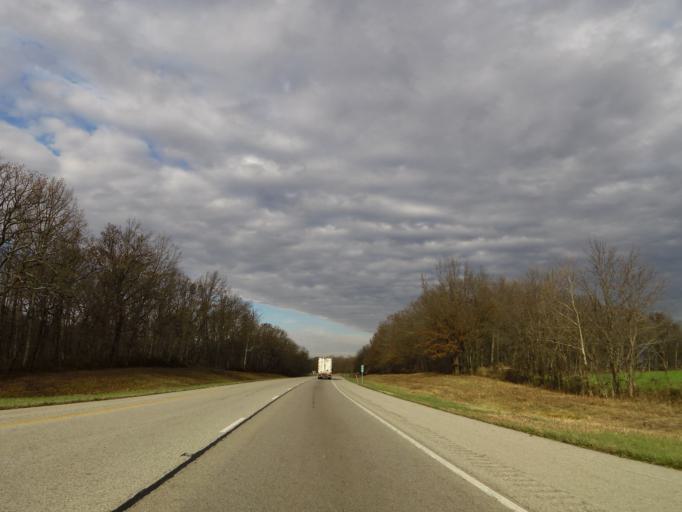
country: US
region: Illinois
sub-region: Washington County
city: Nashville
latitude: 38.4031
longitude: -89.4028
